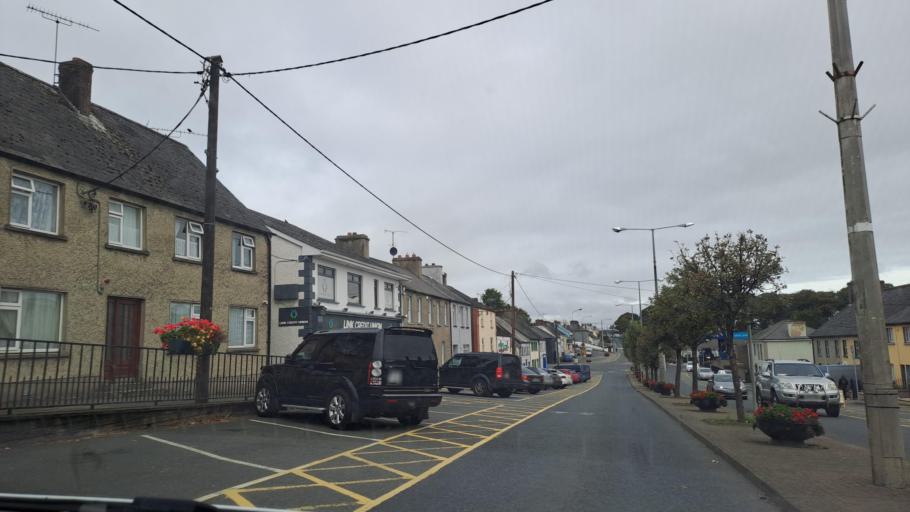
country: IE
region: Ulster
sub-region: An Cabhan
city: Kingscourt
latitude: 53.9068
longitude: -6.8051
